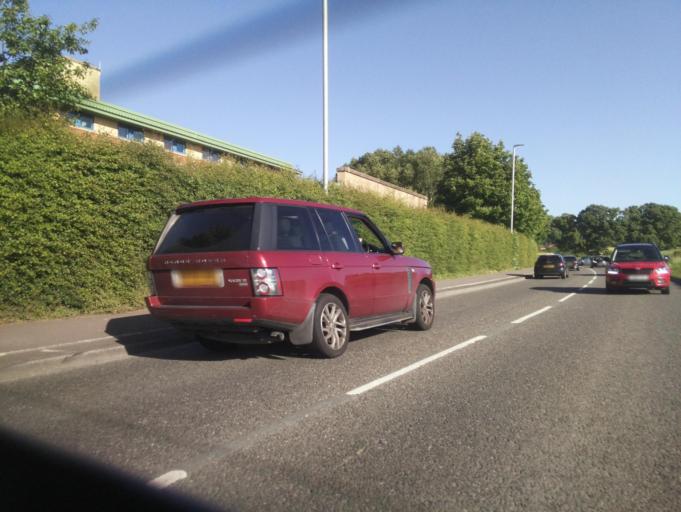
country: GB
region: England
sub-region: Somerset
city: Yeovil
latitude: 50.9354
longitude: -2.6682
